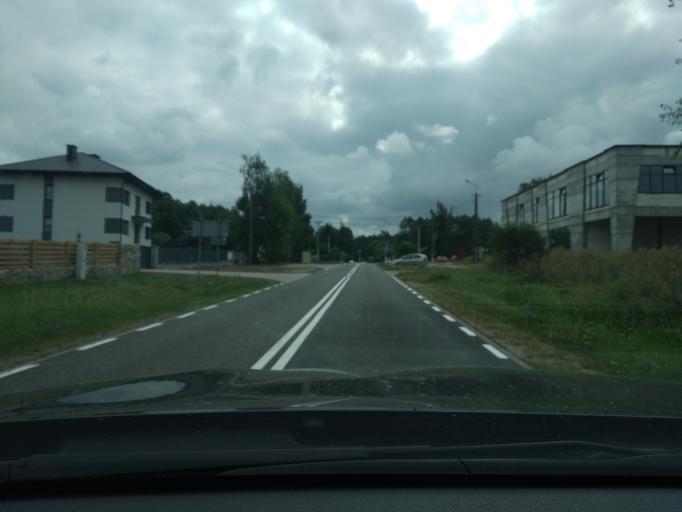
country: PL
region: Masovian Voivodeship
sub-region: Powiat pultuski
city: Obryte
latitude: 52.6478
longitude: 21.2505
